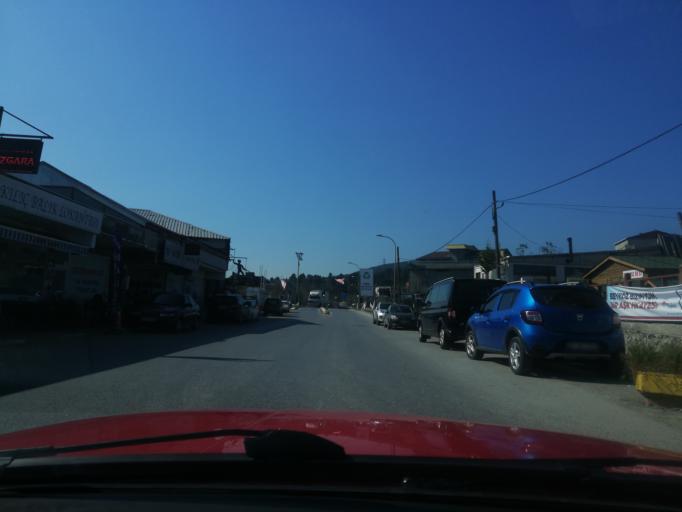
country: TR
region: Istanbul
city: Umraniye
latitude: 41.0831
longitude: 29.1374
